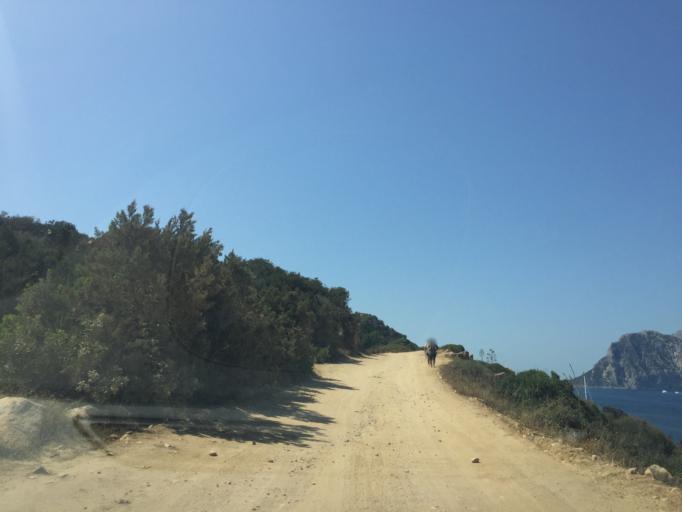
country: IT
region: Sardinia
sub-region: Provincia di Olbia-Tempio
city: San Teodoro
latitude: 40.8409
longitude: 9.7171
